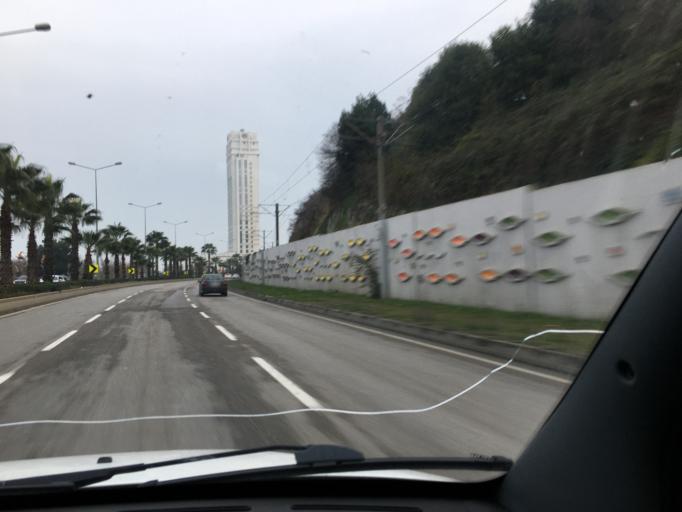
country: TR
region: Samsun
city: Samsun
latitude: 41.3166
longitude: 36.3335
